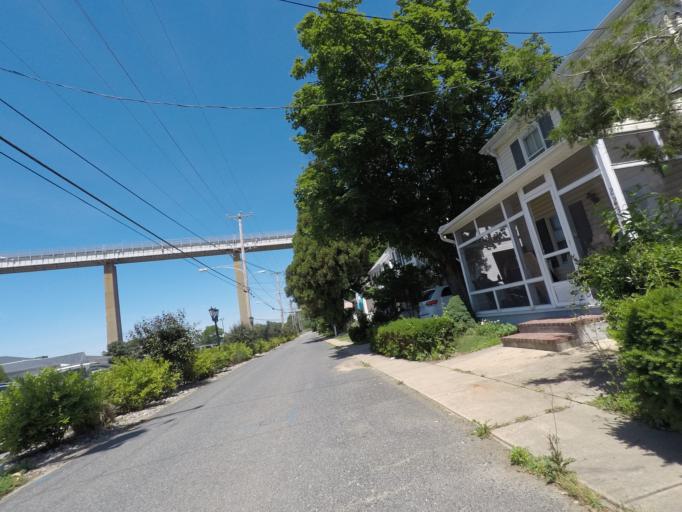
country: US
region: Maryland
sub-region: Cecil County
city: Elkton
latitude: 39.5303
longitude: -75.8120
